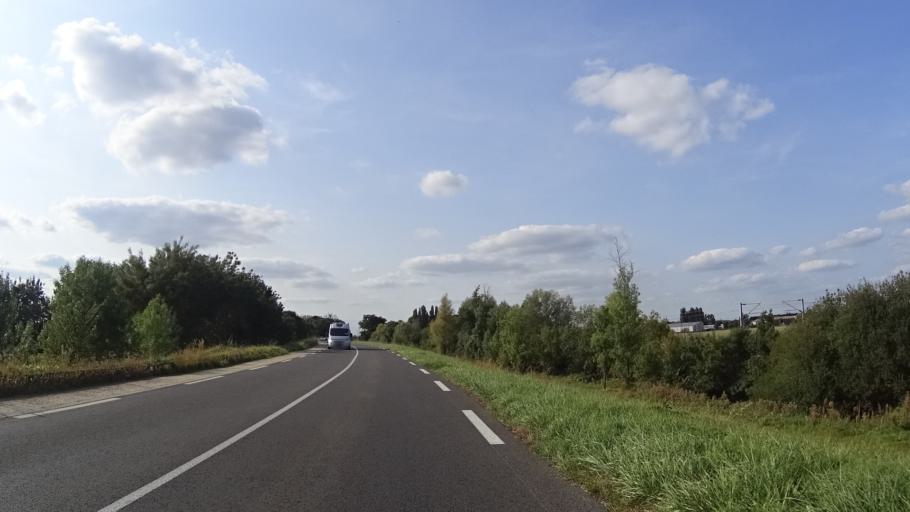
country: FR
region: Pays de la Loire
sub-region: Departement de Maine-et-Loire
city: La Menitre
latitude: 47.4060
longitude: -0.2909
